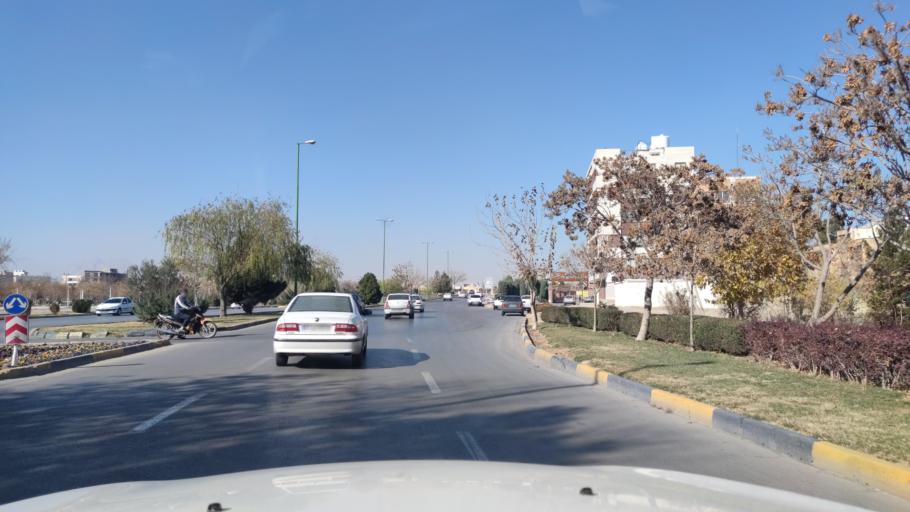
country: IR
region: Isfahan
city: Isfahan
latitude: 32.6814
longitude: 51.6476
